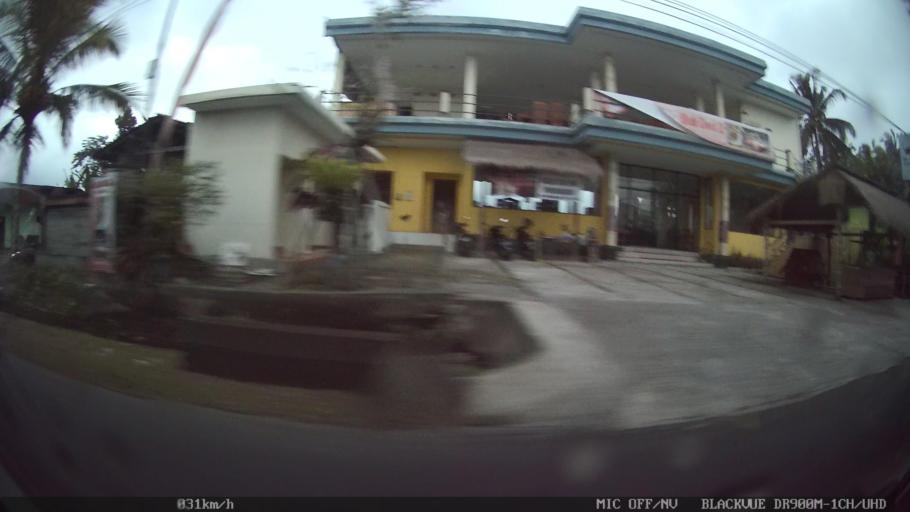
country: ID
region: Bali
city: Banjar Buahan
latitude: -8.4063
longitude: 115.2460
